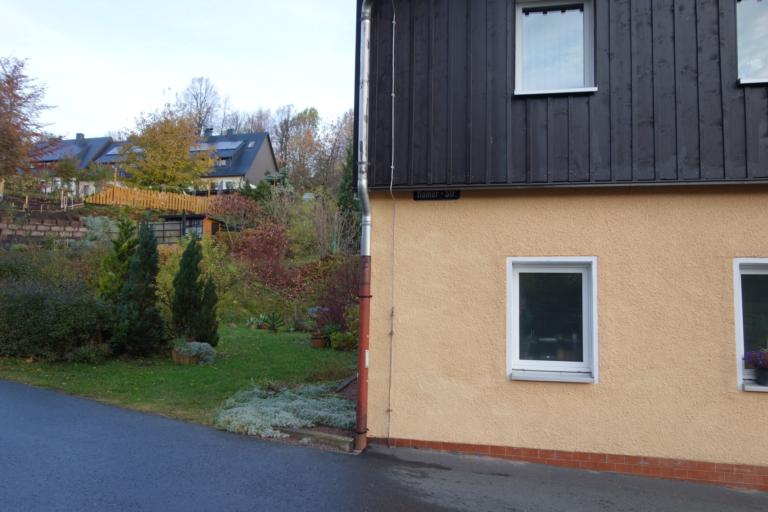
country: DE
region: Saxony
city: Altenberg
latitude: 50.7633
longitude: 13.7629
